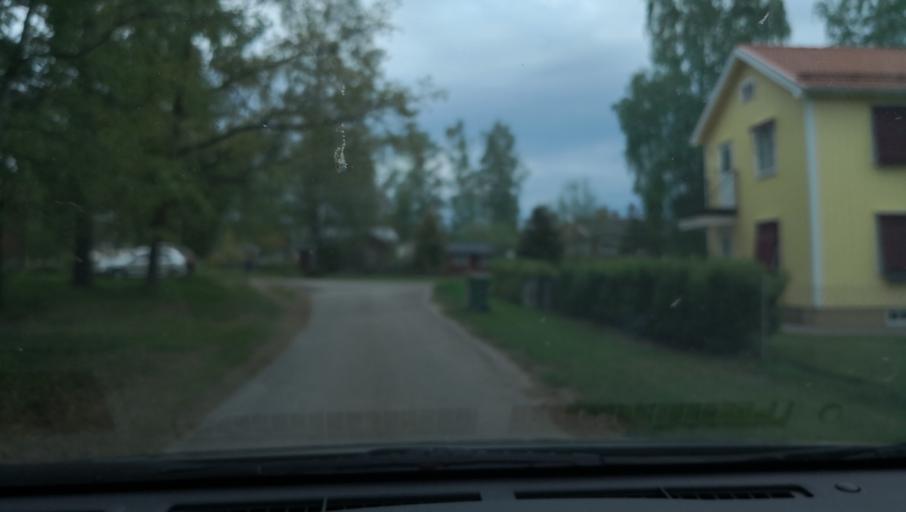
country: SE
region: Vaestmanland
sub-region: Skinnskattebergs Kommun
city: Skinnskatteberg
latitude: 59.8066
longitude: 15.5512
